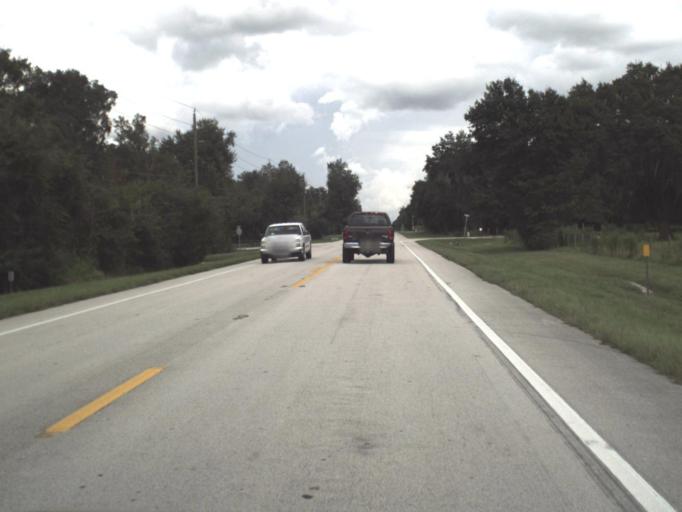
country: US
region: Florida
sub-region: DeSoto County
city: Arcadia
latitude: 27.2160
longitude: -81.9050
